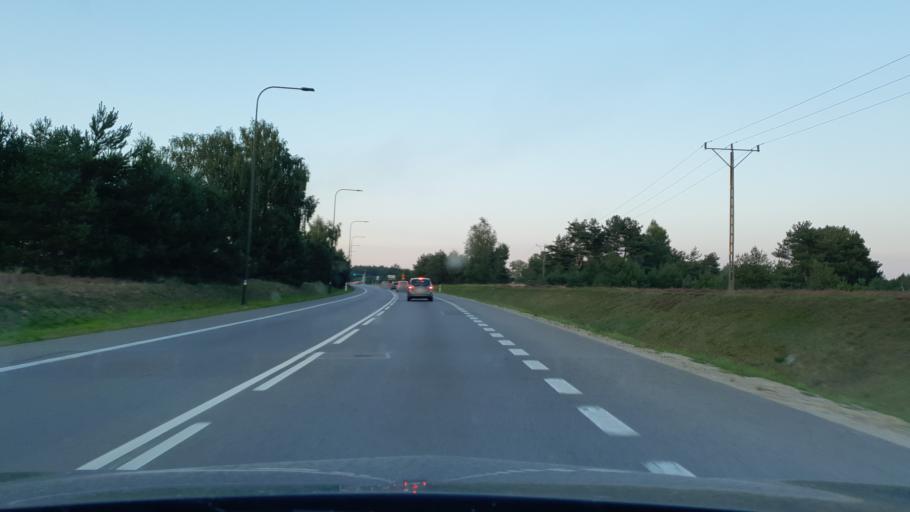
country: PL
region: Pomeranian Voivodeship
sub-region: Powiat leborski
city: Lebork
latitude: 54.5422
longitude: 17.7847
